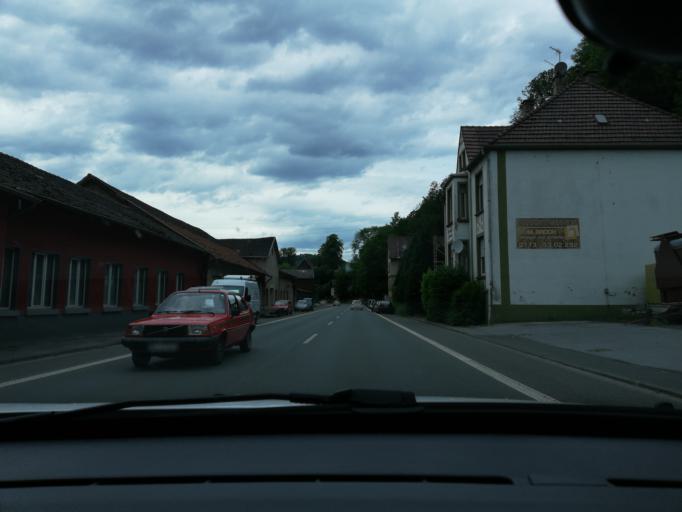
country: DE
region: North Rhine-Westphalia
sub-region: Regierungsbezirk Arnsberg
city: Schalksmuhle
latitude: 51.3095
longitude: 7.5308
